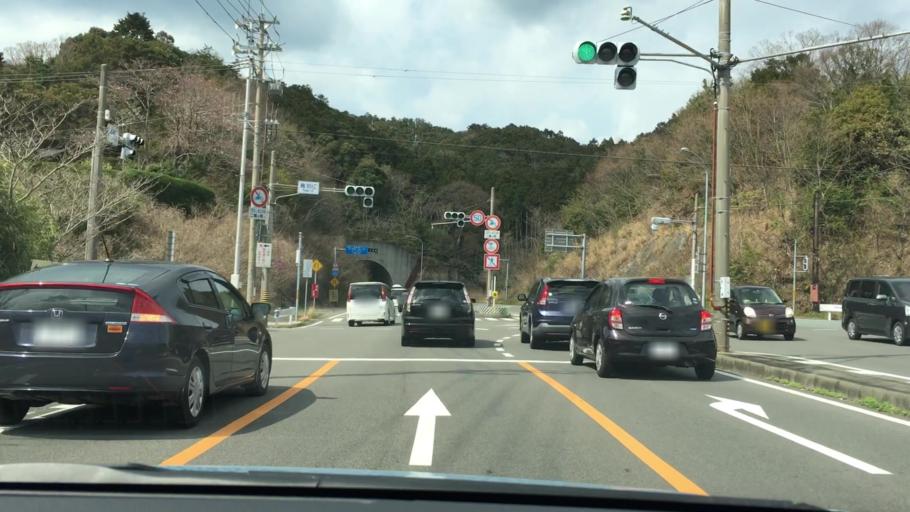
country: JP
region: Mie
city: Toba
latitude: 34.4858
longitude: 136.8158
